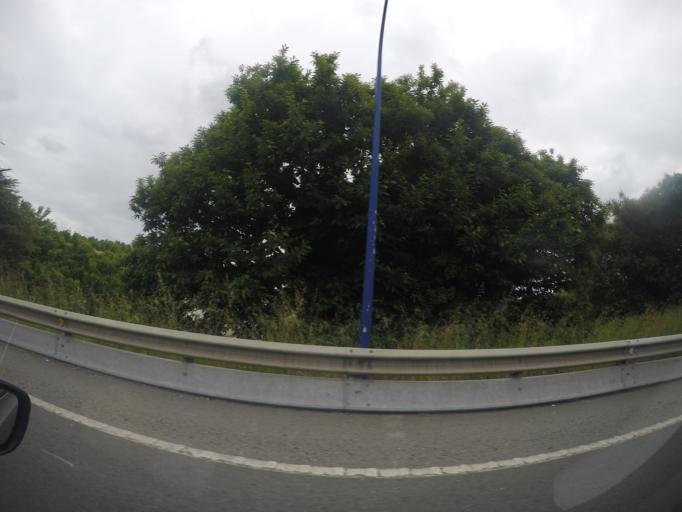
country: ES
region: Galicia
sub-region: Provincia da Coruna
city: Culleredo
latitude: 43.3064
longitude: -8.3810
